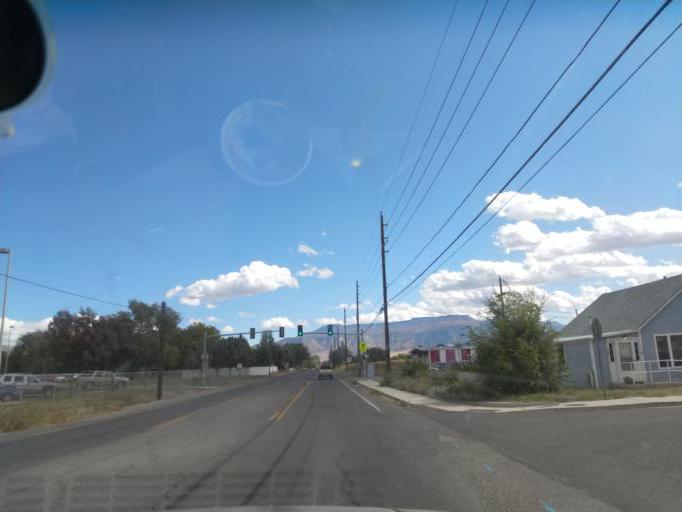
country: US
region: Colorado
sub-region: Mesa County
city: Clifton
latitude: 39.0918
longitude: -108.4461
